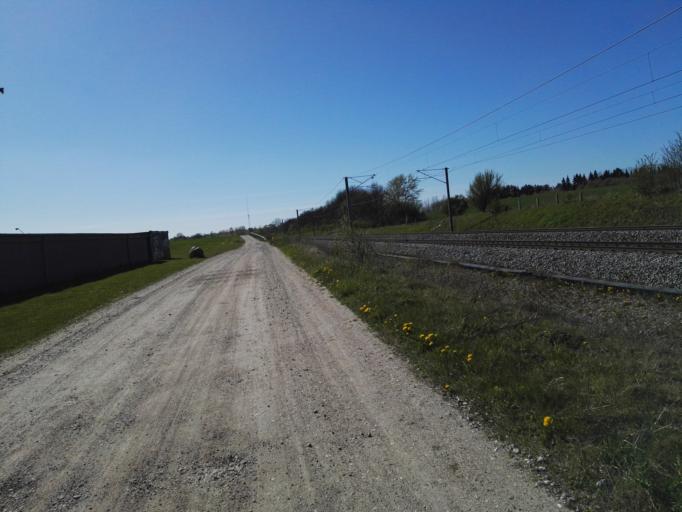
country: DK
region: Capital Region
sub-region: Egedal Kommune
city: Smorumnedre
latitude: 55.7523
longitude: 12.2795
